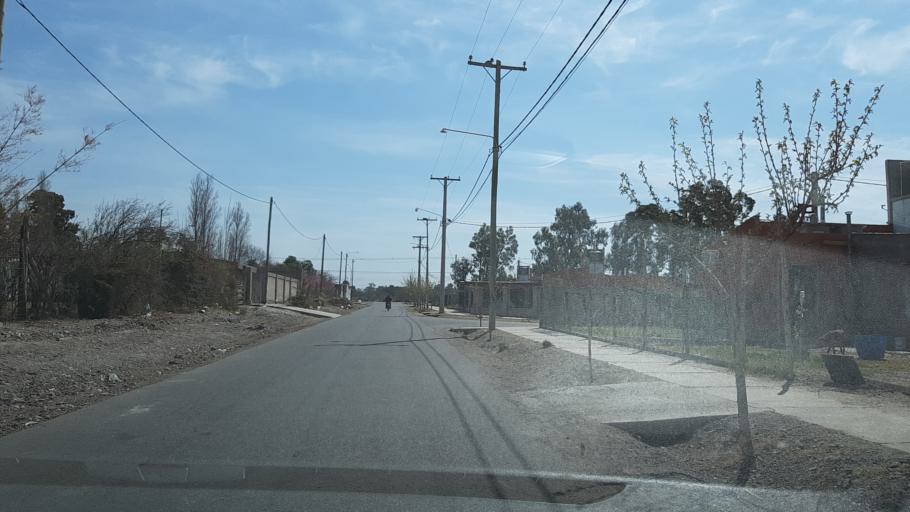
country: AR
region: San Juan
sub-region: Departamento de Zonda
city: Zonda
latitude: -31.5454
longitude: -68.7418
